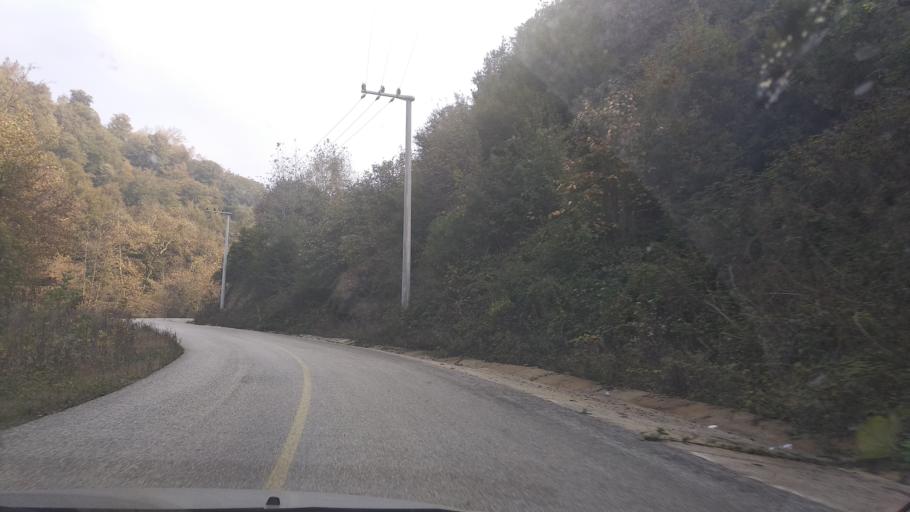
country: TR
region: Duzce
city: Kaynasli
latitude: 40.7323
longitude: 31.2257
